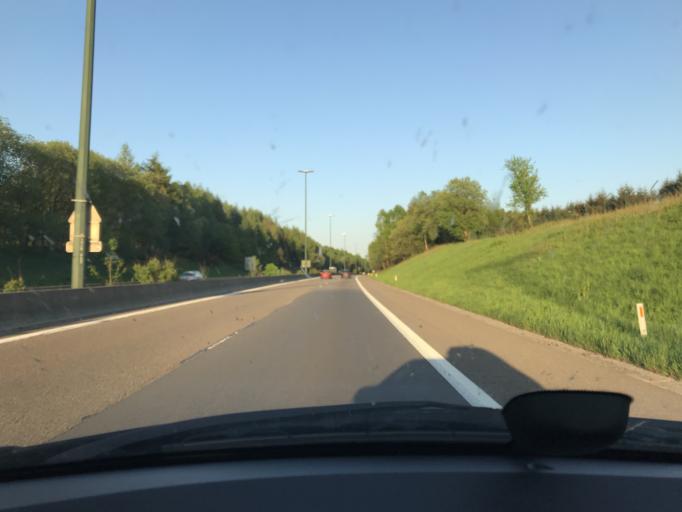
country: BE
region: Wallonia
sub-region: Province du Luxembourg
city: Neufchateau
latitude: 49.8843
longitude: 5.4184
